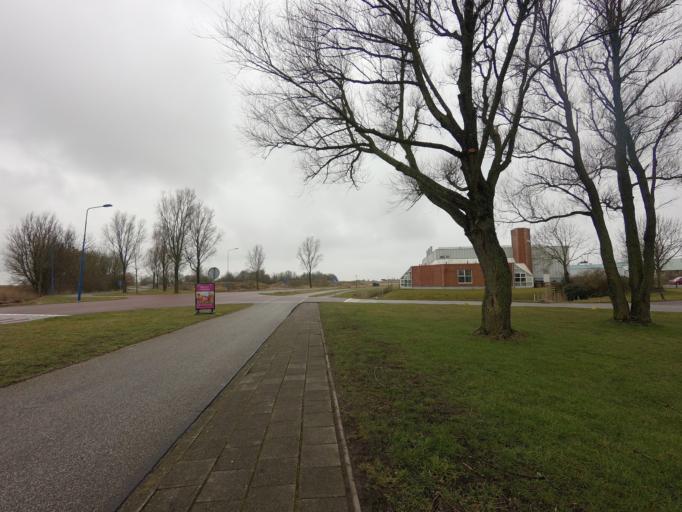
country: NL
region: Friesland
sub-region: Sudwest Fryslan
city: Makkum
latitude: 53.0495
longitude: 5.4019
